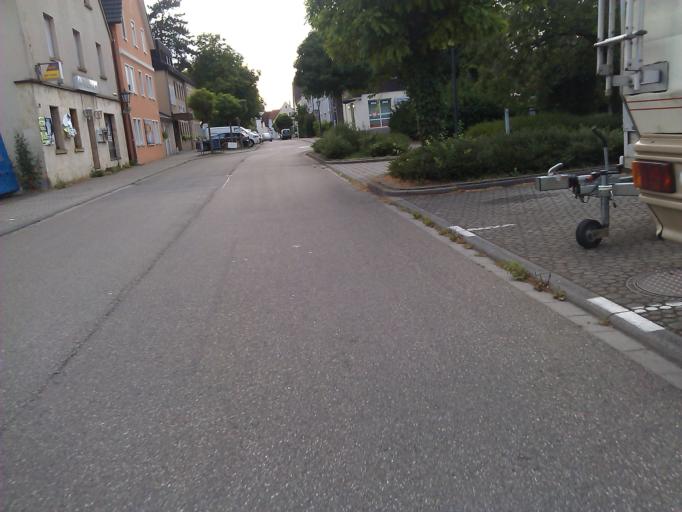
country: DE
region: Baden-Wuerttemberg
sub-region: Regierungsbezirk Stuttgart
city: Untereisesheim
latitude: 49.2328
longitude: 9.1930
